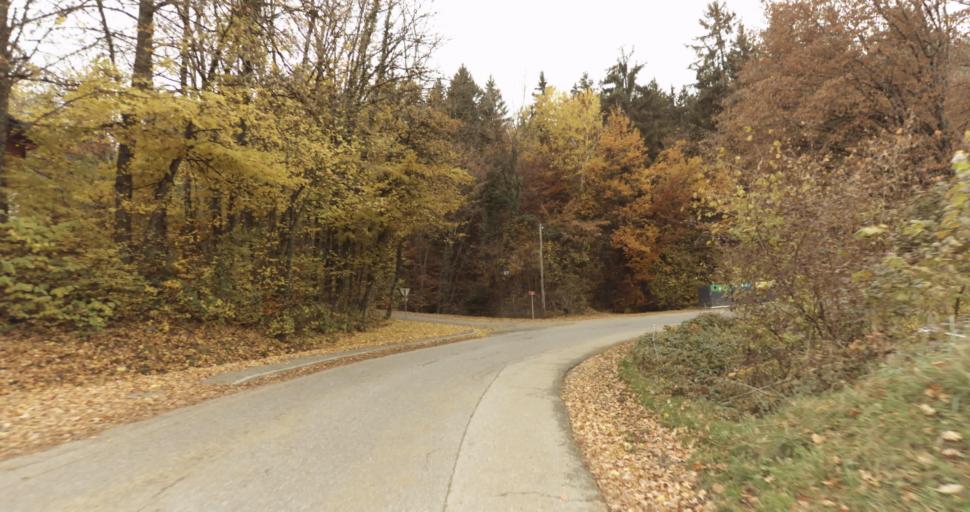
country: FR
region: Rhone-Alpes
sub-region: Departement de la Haute-Savoie
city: Saint-Martin-Bellevue
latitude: 45.9530
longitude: 6.1545
